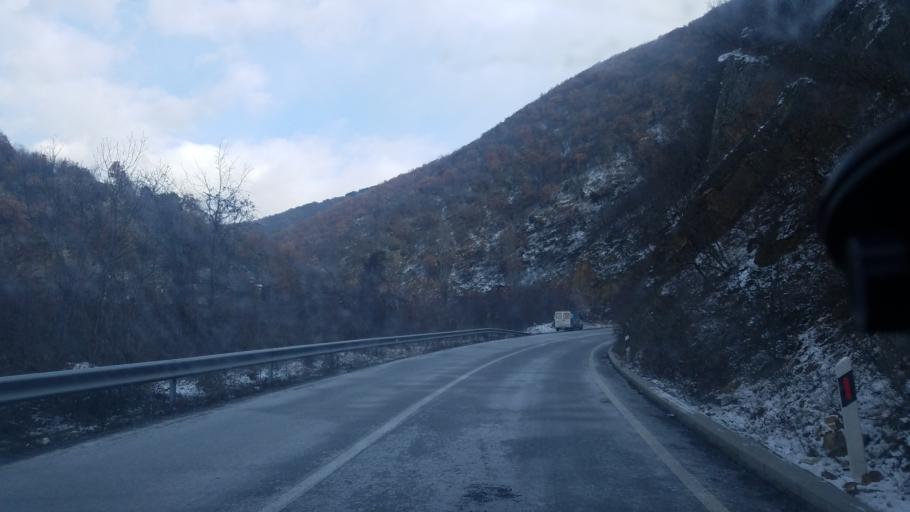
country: MK
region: Vinica
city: Vinica
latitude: 41.9410
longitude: 22.5268
